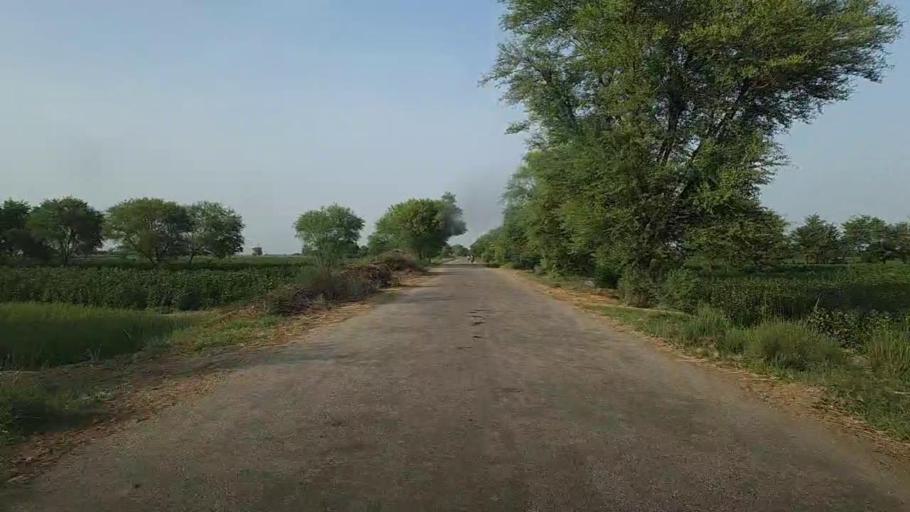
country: PK
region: Sindh
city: Ubauro
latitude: 28.1100
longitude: 69.8181
